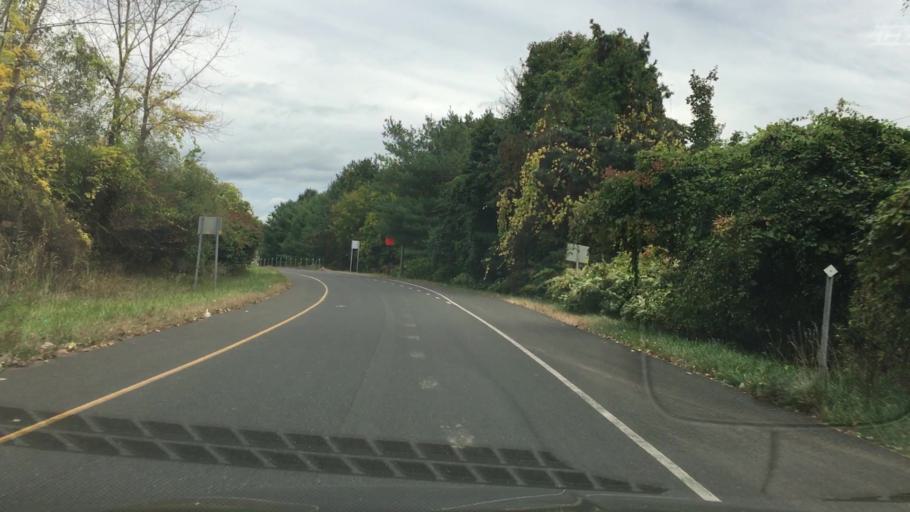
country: US
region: Connecticut
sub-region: Hartford County
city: Hartford
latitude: 41.7568
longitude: -72.6456
